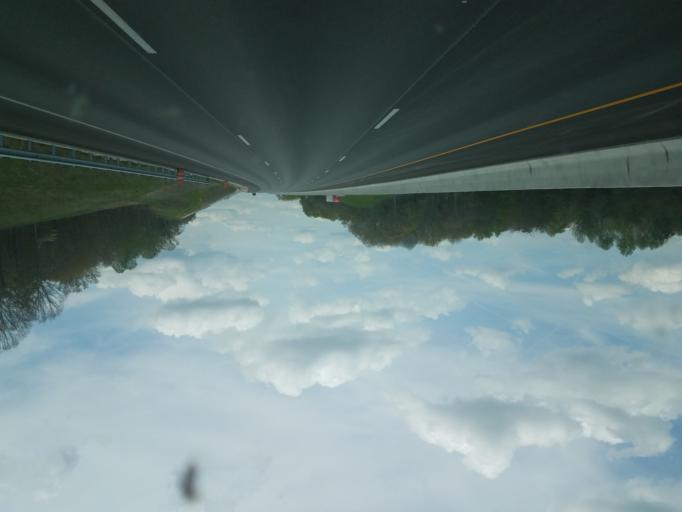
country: US
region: Kentucky
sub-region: Hart County
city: Munfordville
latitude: 37.3390
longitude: -85.9066
